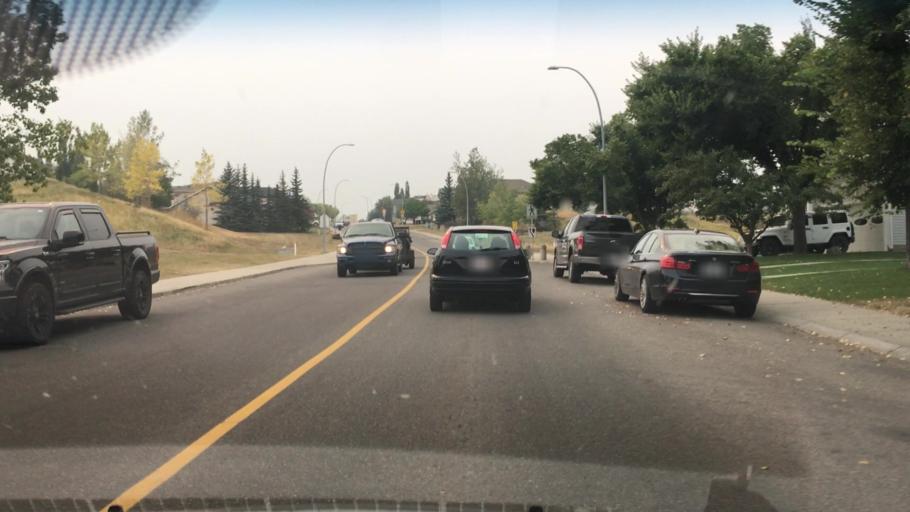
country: CA
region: Alberta
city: Calgary
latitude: 51.1516
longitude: -114.1124
